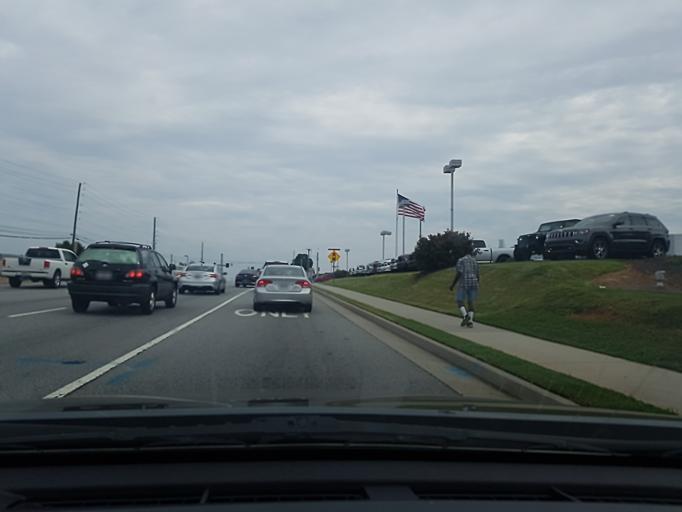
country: US
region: Georgia
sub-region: Gwinnett County
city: Duluth
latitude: 33.9673
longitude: -84.1437
